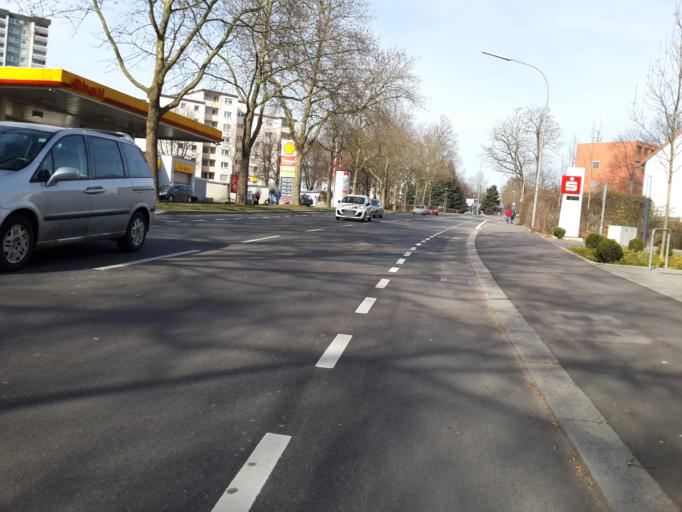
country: DE
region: Baden-Wuerttemberg
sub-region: Regierungsbezirk Stuttgart
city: Heilbronn
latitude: 49.1450
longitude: 9.1862
